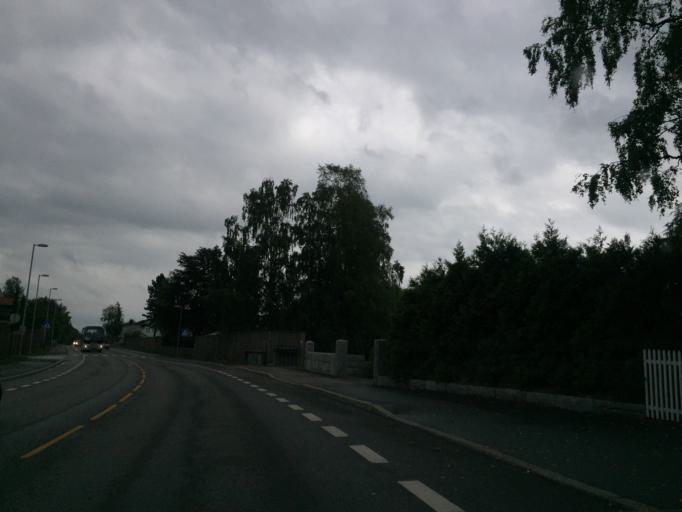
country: NO
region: Oslo
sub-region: Oslo
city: Sjolyststranda
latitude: 59.9472
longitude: 10.6766
